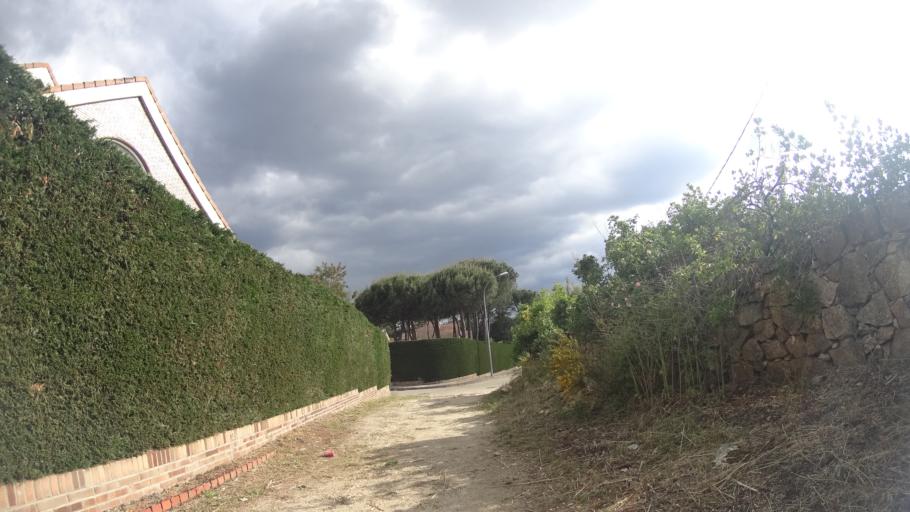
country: ES
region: Madrid
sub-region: Provincia de Madrid
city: Galapagar
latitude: 40.5729
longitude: -3.9869
